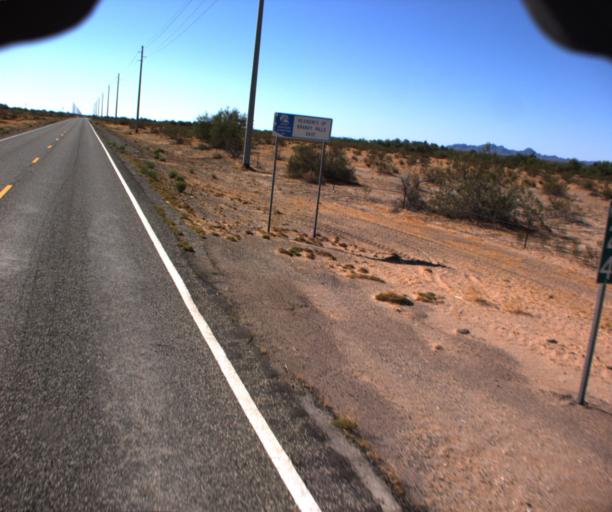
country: US
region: Arizona
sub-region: La Paz County
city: Cienega Springs
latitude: 33.9670
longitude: -114.0383
